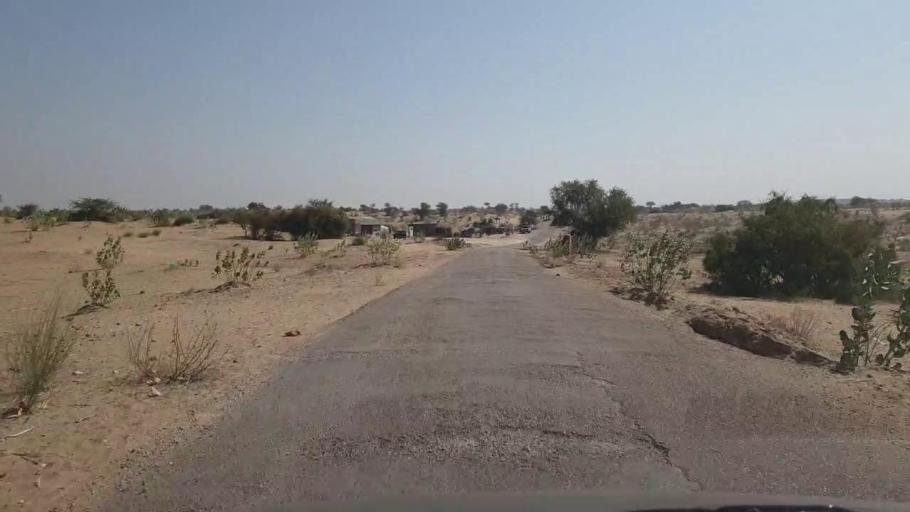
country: PK
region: Sindh
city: Chor
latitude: 25.6007
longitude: 70.0009
